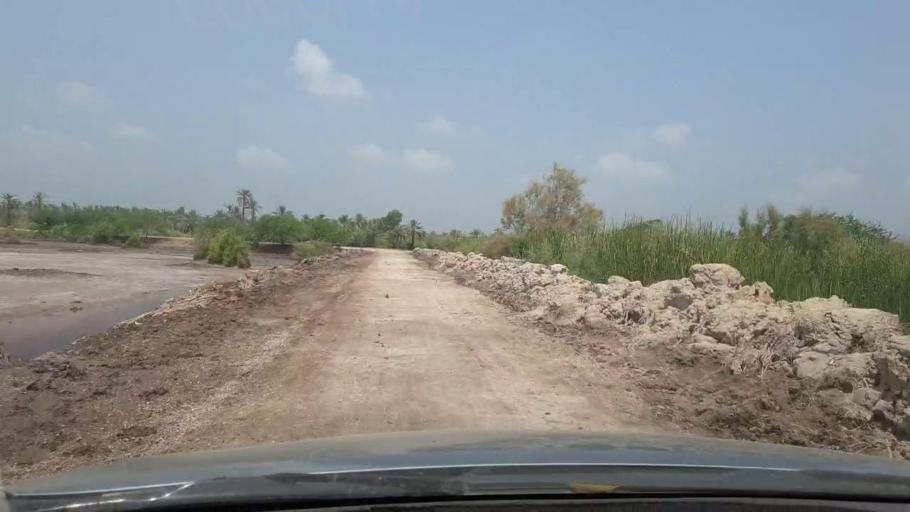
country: PK
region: Sindh
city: Khairpur
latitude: 27.4789
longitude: 68.6915
